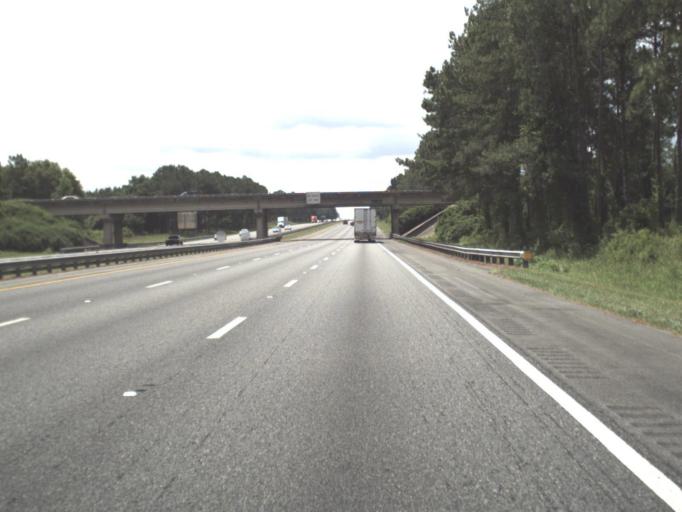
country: US
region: Florida
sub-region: Columbia County
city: Lake City
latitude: 30.1661
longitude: -82.6818
